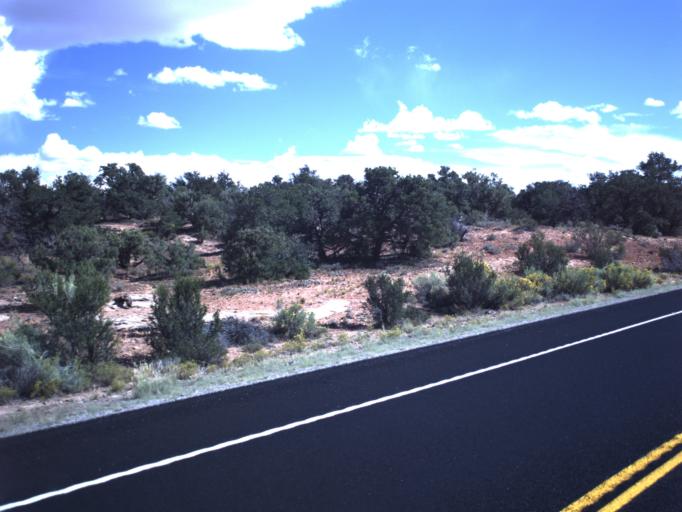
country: US
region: Utah
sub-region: Grand County
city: Moab
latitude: 38.5557
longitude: -109.7926
